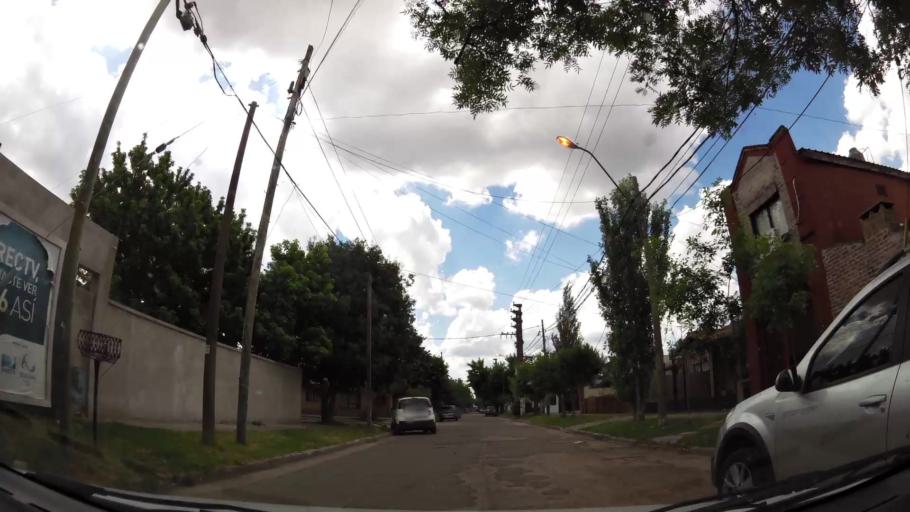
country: AR
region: Buenos Aires
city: Ituzaingo
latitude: -34.6520
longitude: -58.6660
